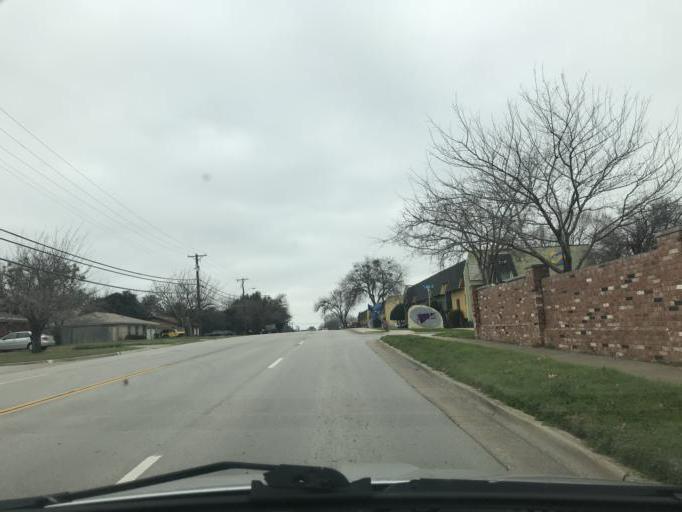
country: US
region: Texas
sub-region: Tarrant County
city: North Richland Hills
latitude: 32.8426
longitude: -97.2091
